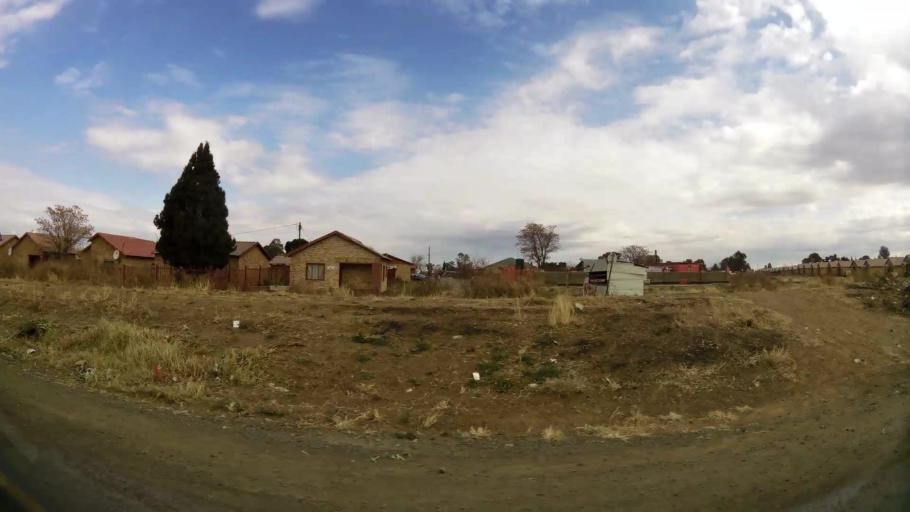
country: ZA
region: Orange Free State
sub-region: Fezile Dabi District Municipality
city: Kroonstad
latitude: -27.6460
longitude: 27.2220
